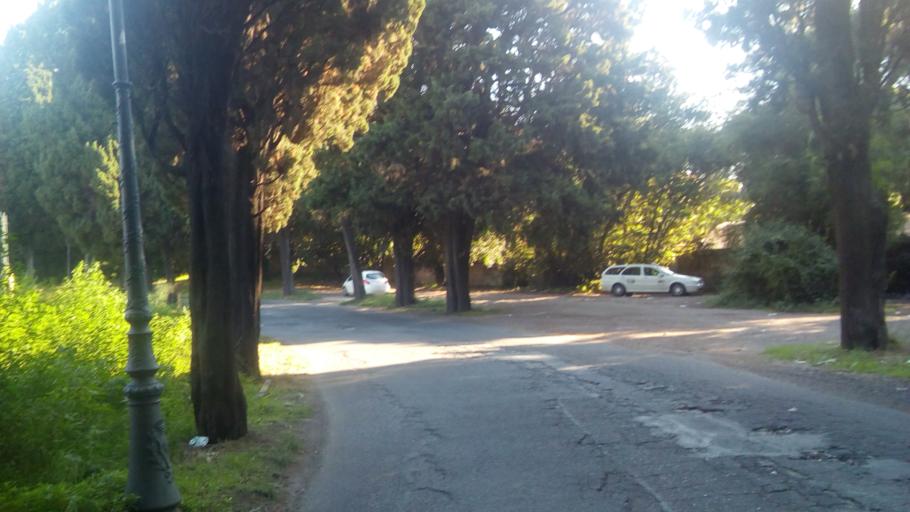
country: IT
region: Latium
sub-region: Citta metropolitana di Roma Capitale
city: Rome
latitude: 41.8772
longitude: 12.4938
